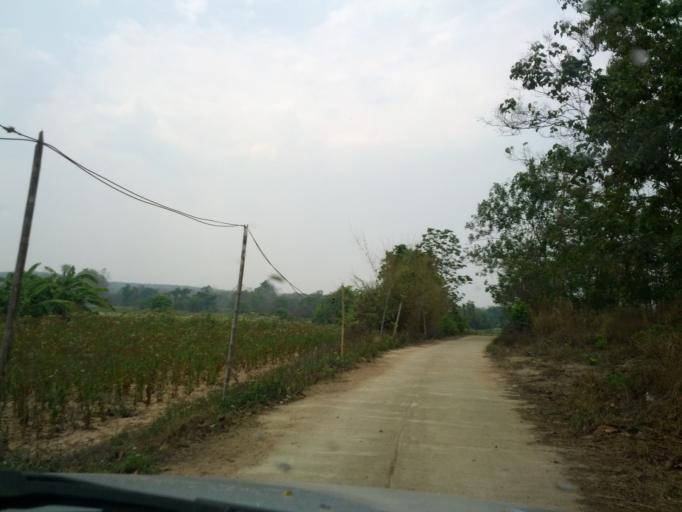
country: TH
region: Chiang Mai
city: Mae Taeng
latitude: 19.1069
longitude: 98.9900
